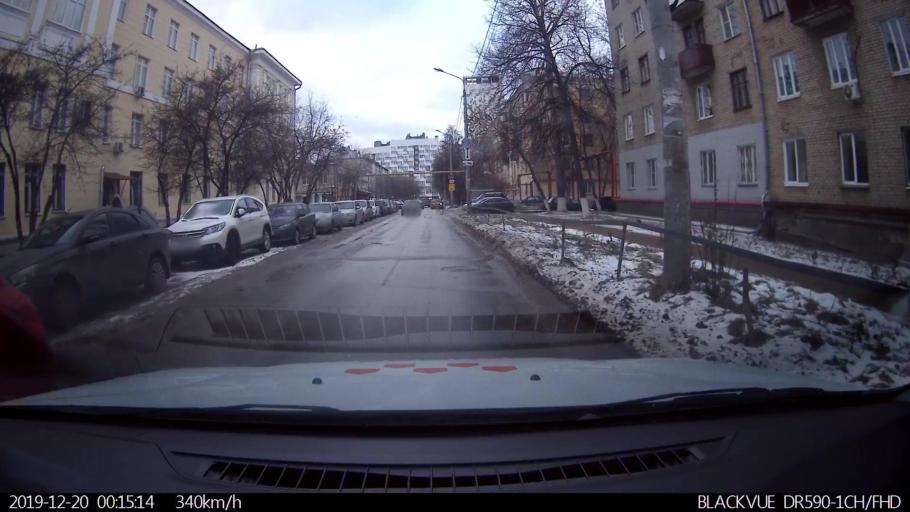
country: RU
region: Jaroslavl
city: Porech'ye-Rybnoye
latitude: 56.9971
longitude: 39.3857
